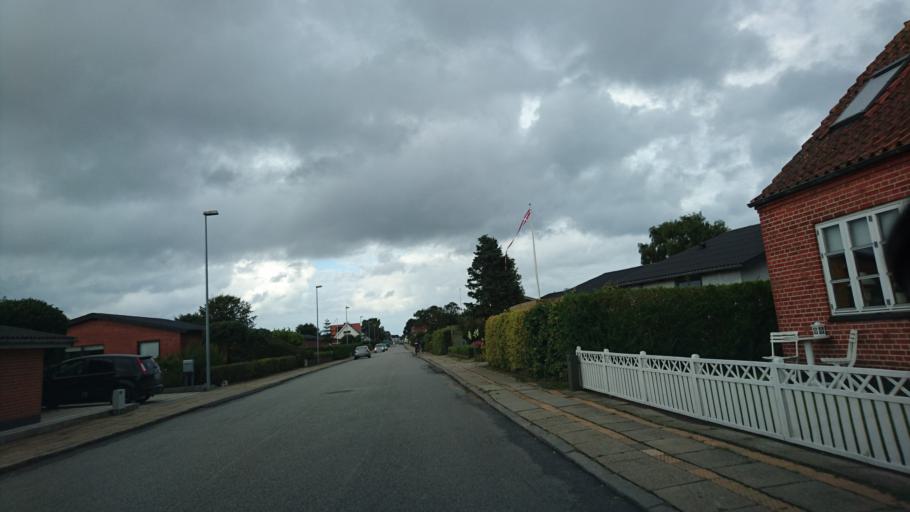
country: DK
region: North Denmark
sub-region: Frederikshavn Kommune
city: Frederikshavn
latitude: 57.4227
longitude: 10.5130
